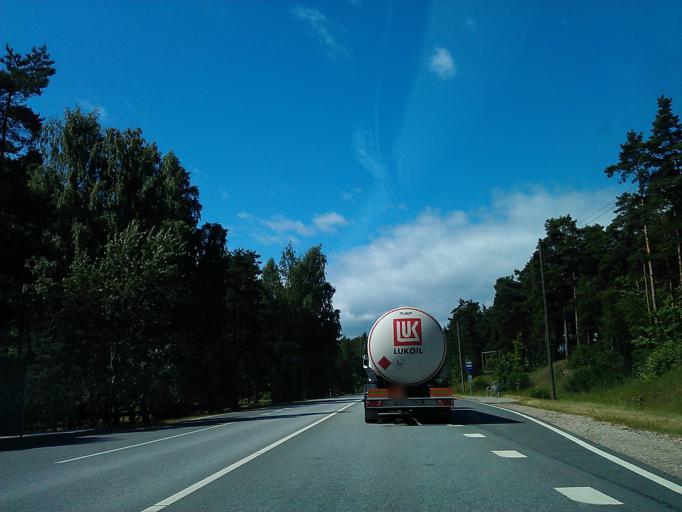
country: LV
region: Jurmala
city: Jurmala
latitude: 56.9296
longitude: 23.6917
